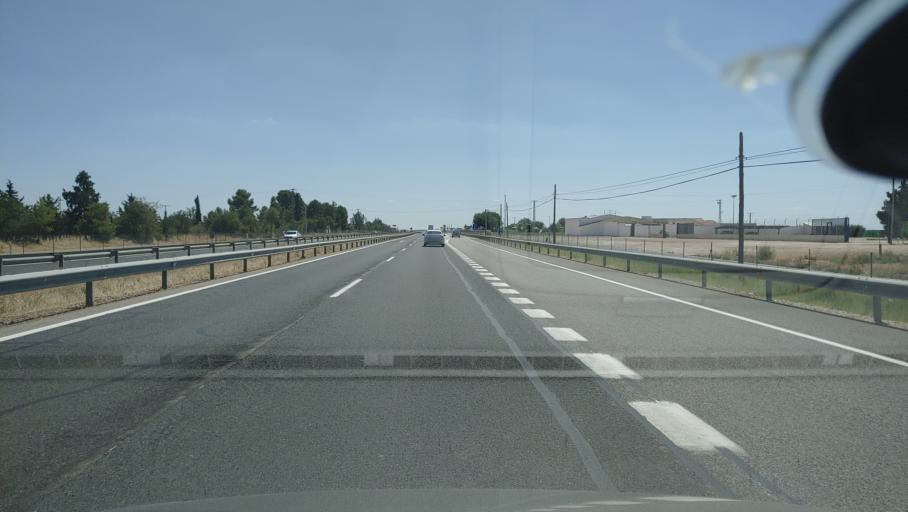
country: ES
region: Castille-La Mancha
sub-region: Provincia de Ciudad Real
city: Manzanares
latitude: 39.1150
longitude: -3.3776
